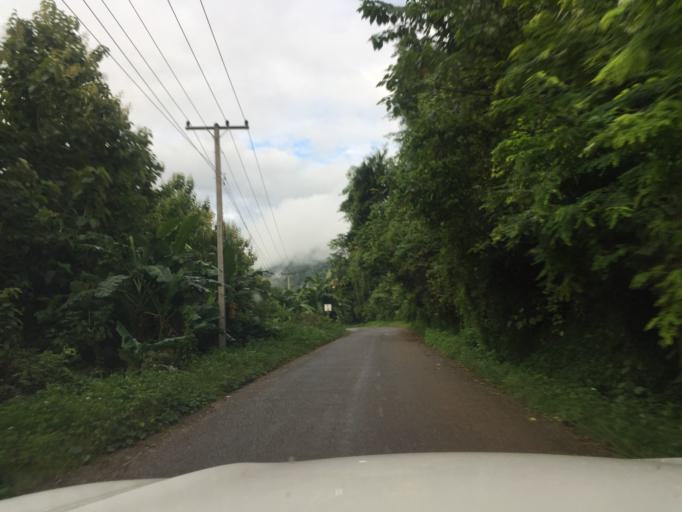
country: LA
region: Phongsali
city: Khoa
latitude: 21.0956
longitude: 102.2499
